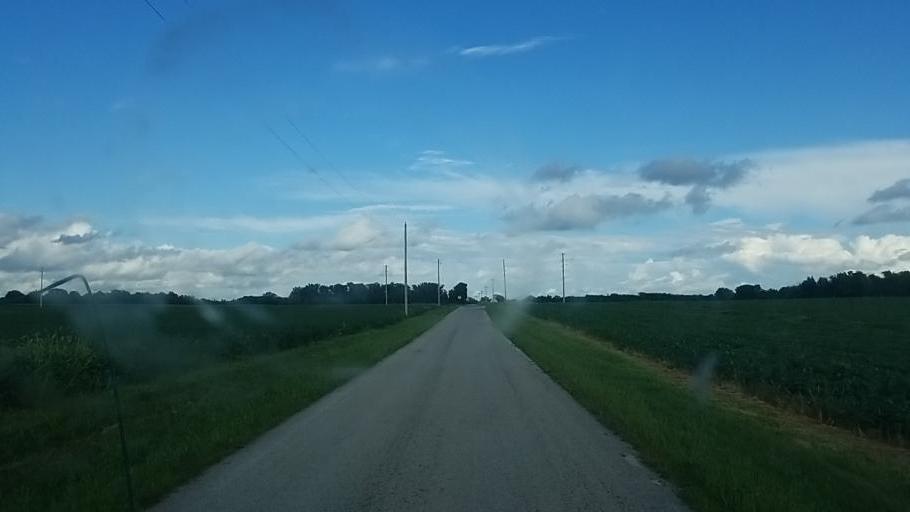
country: US
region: Ohio
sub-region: Hardin County
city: Forest
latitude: 40.7885
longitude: -83.4214
